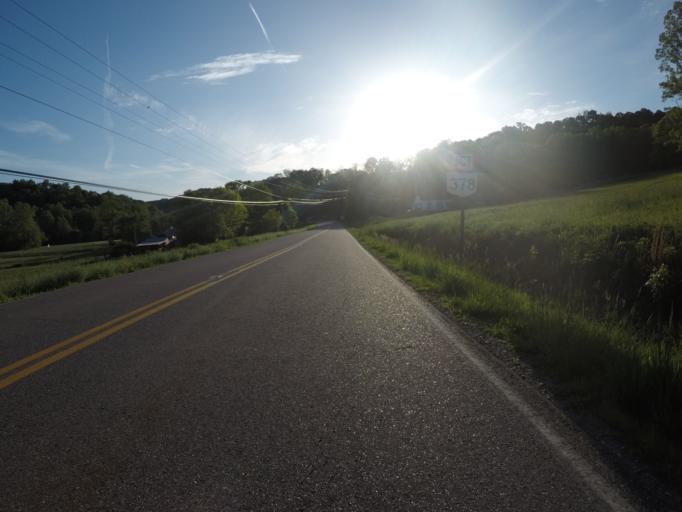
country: US
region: West Virginia
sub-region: Cabell County
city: Huntington
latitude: 38.5542
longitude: -82.4614
